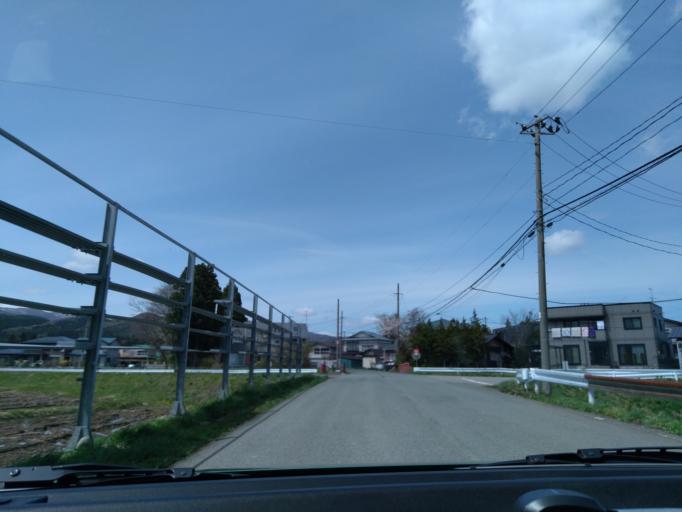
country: JP
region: Iwate
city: Kitakami
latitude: 39.3048
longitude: 140.9749
